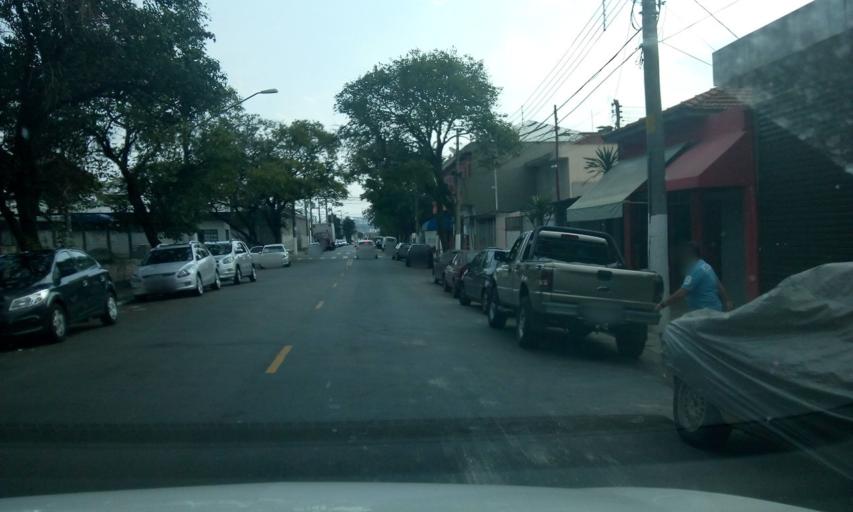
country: BR
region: Sao Paulo
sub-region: Osasco
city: Osasco
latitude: -23.5304
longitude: -46.7346
